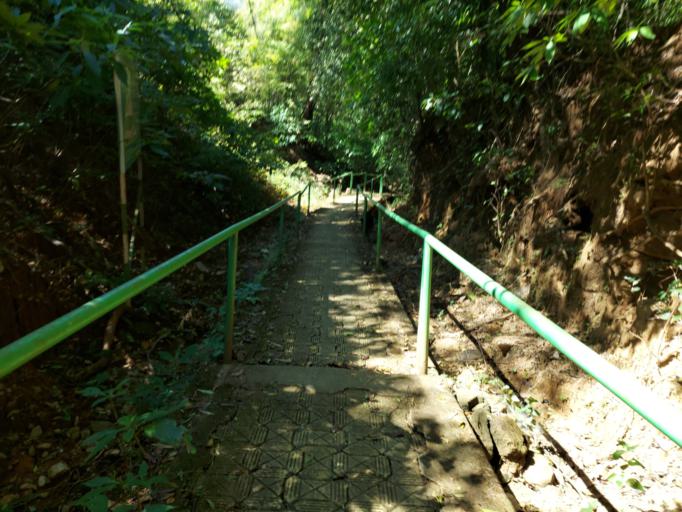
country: IN
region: Maharashtra
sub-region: Sindhudurg
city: Kudal
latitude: 16.0823
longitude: 73.8286
